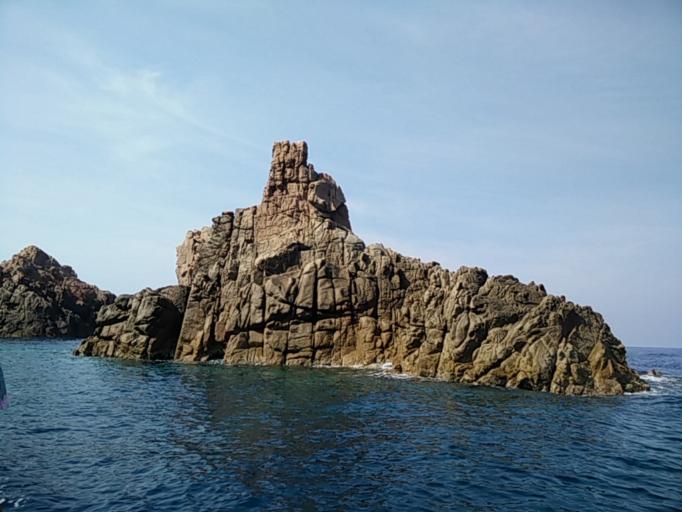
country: FR
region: Corsica
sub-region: Departement de la Corse-du-Sud
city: Cargese
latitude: 42.2372
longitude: 8.5395
